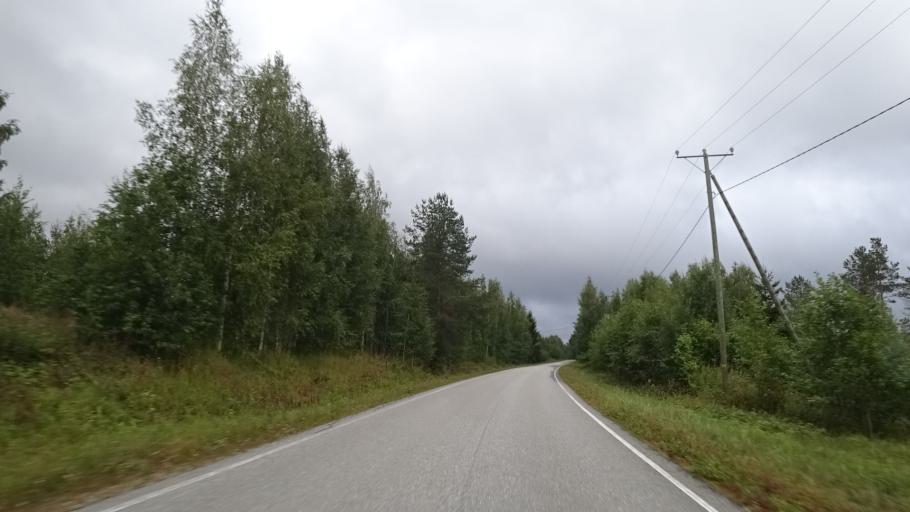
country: FI
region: North Karelia
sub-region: Joensuu
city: Ilomantsi
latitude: 63.2472
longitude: 30.7657
